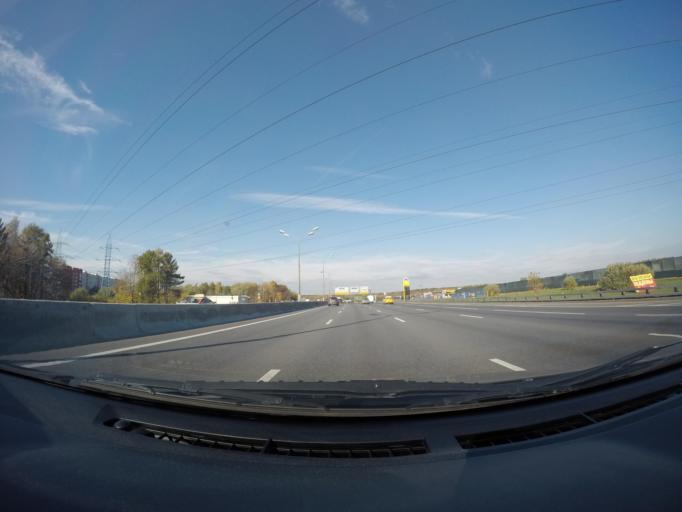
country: RU
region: Moscow
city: Gol'yanovo
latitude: 55.8242
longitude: 37.8355
